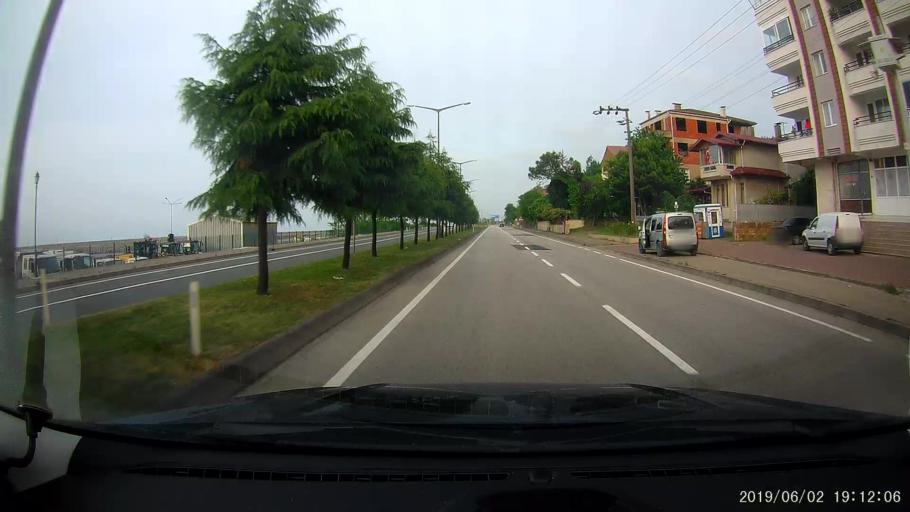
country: TR
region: Ordu
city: Gulyali
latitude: 40.9662
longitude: 38.0632
